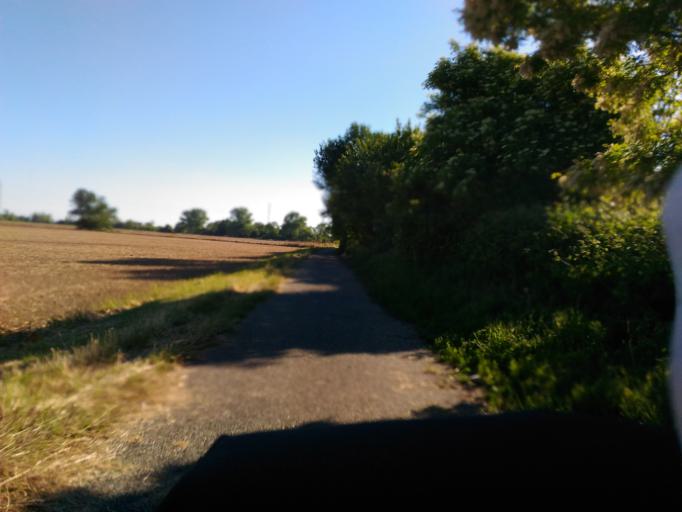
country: IT
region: Lombardy
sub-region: Citta metropolitana di Milano
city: Civesio
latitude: 45.3790
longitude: 9.2620
